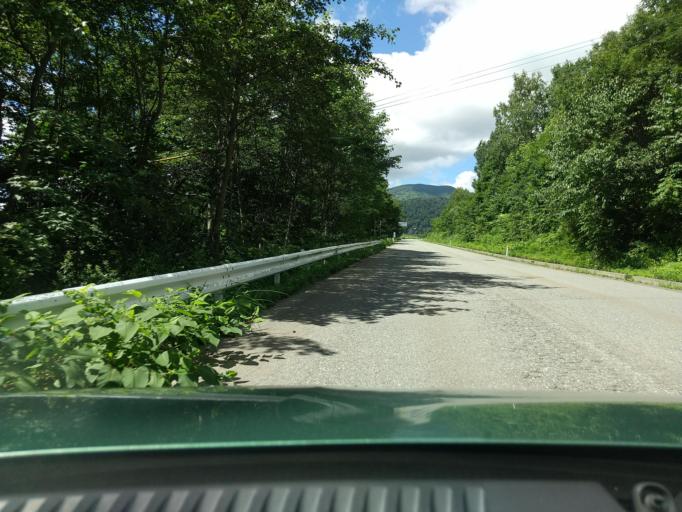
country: JP
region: Iwate
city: Shizukuishi
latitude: 39.7752
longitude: 140.7638
